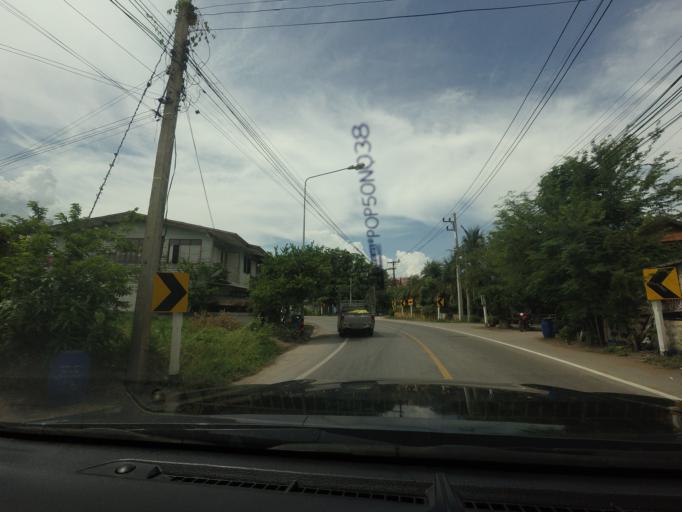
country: TH
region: Kanchanaburi
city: Phanom Thuan
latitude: 14.1039
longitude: 99.6582
